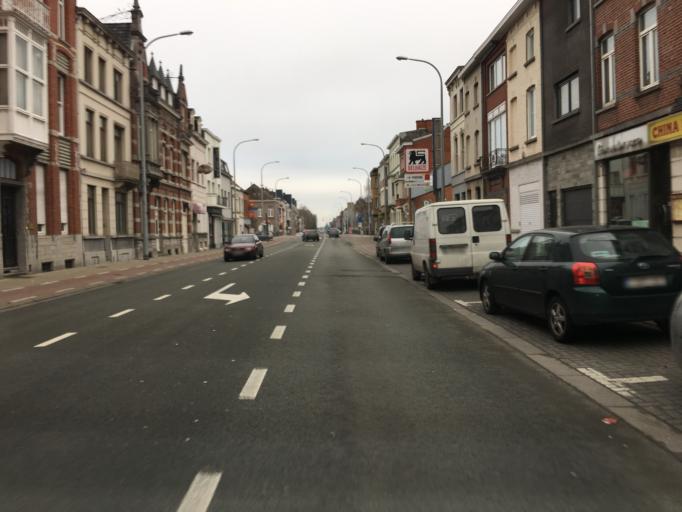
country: BE
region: Flanders
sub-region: Provincie West-Vlaanderen
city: Kortrijk
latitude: 50.8322
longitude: 3.2758
